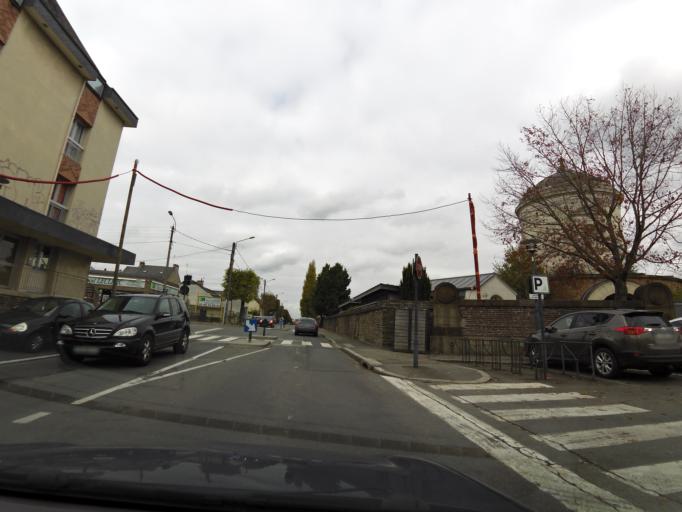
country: FR
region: Brittany
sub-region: Departement d'Ille-et-Vilaine
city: Rennes
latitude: 48.1244
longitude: -1.6817
